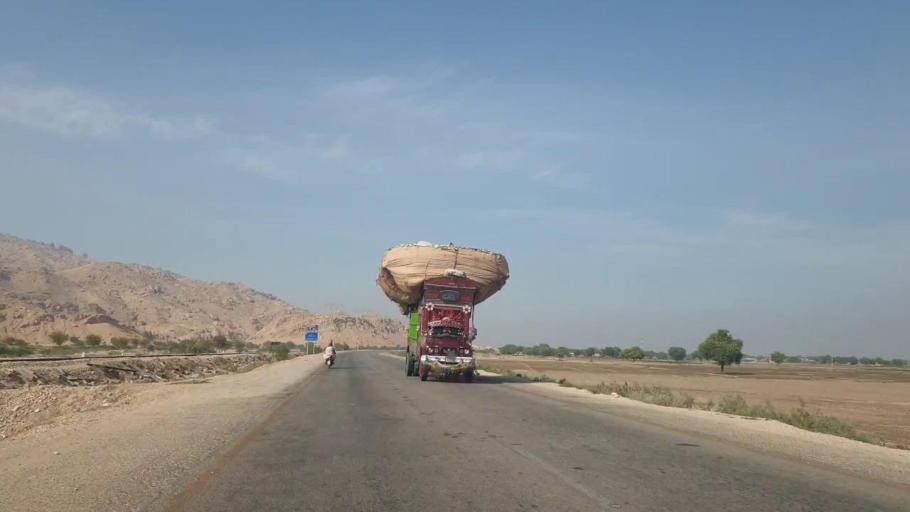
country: PK
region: Sindh
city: Sehwan
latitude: 26.2844
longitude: 67.8952
